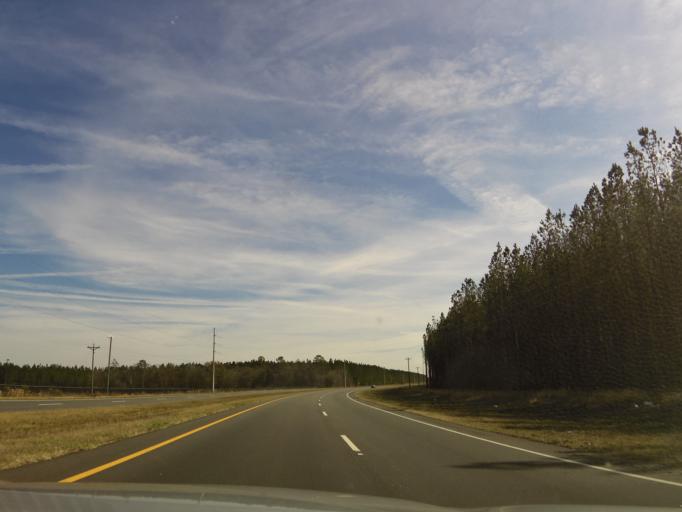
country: US
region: Georgia
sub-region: Glynn County
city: Dock Junction
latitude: 31.2327
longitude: -81.7479
